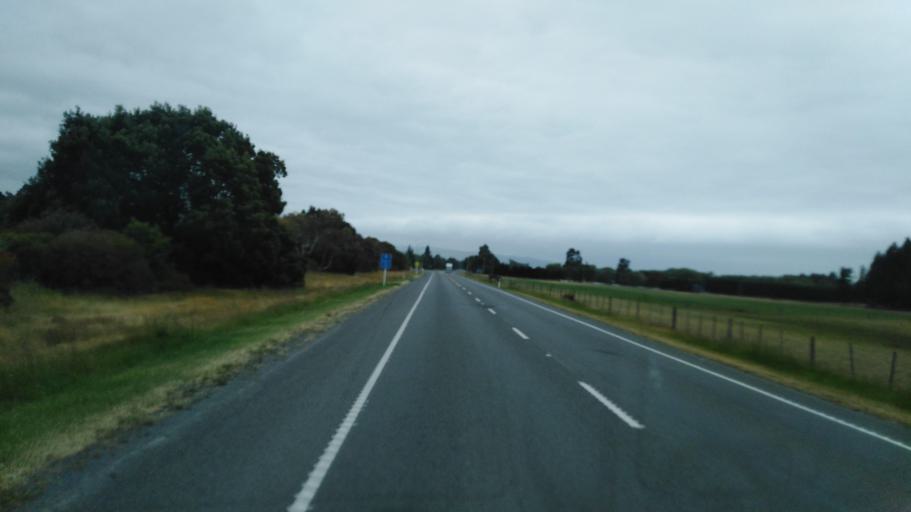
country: NZ
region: Canterbury
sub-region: Hurunui District
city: Amberley
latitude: -43.2065
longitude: 172.7394
